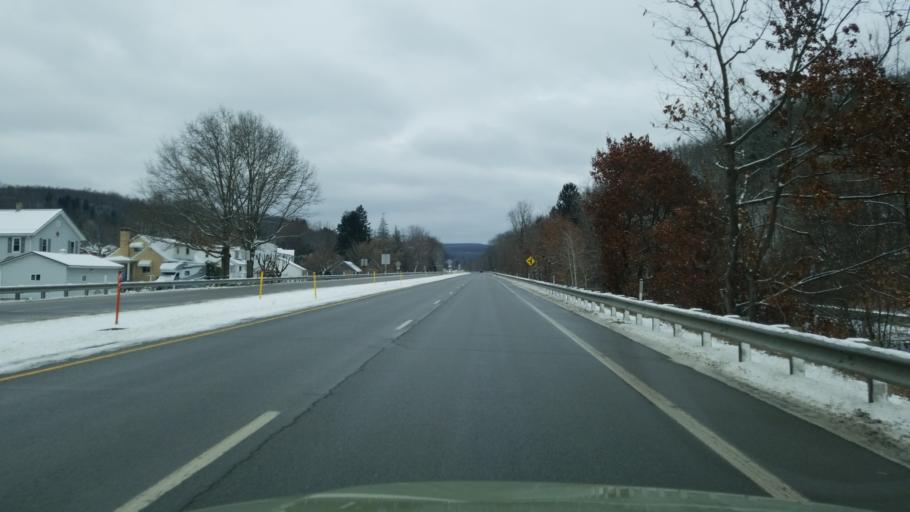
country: US
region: Pennsylvania
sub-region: Clearfield County
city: Clearfield
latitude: 41.0346
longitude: -78.4466
